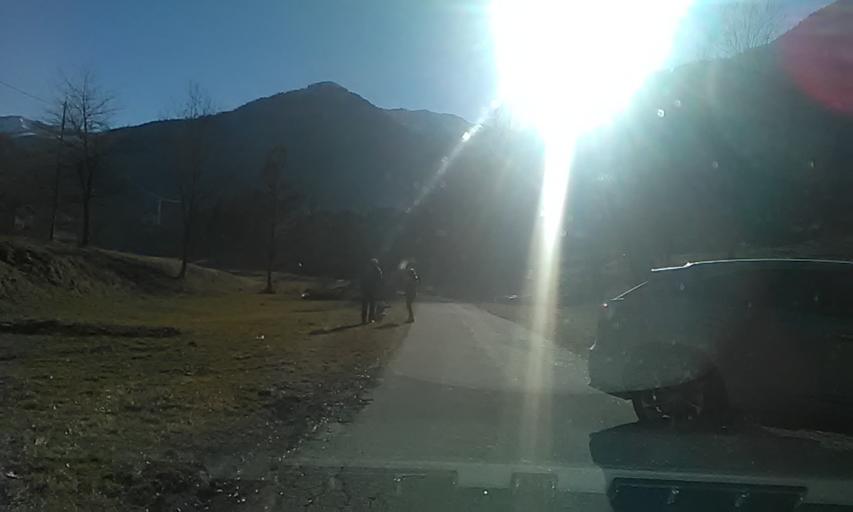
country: IT
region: Piedmont
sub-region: Provincia di Vercelli
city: Piode
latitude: 45.7823
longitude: 8.0397
